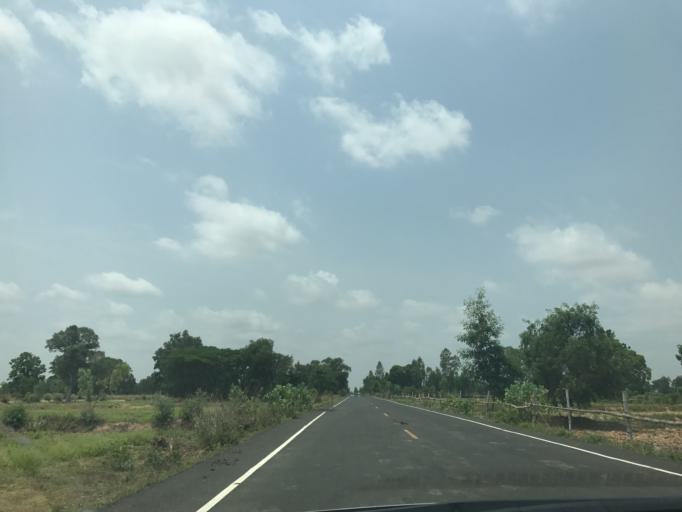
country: TH
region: Surin
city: Chom Phra
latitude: 15.0596
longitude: 103.6609
